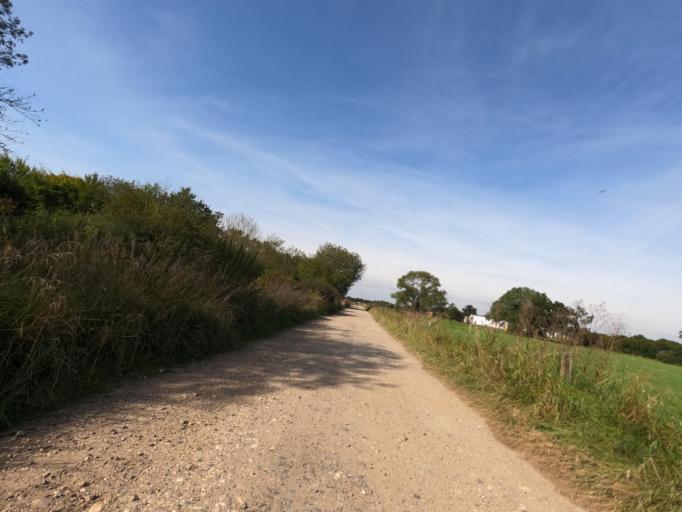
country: DE
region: North Rhine-Westphalia
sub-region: Regierungsbezirk Koln
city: Linnich
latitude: 50.9702
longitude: 6.2919
